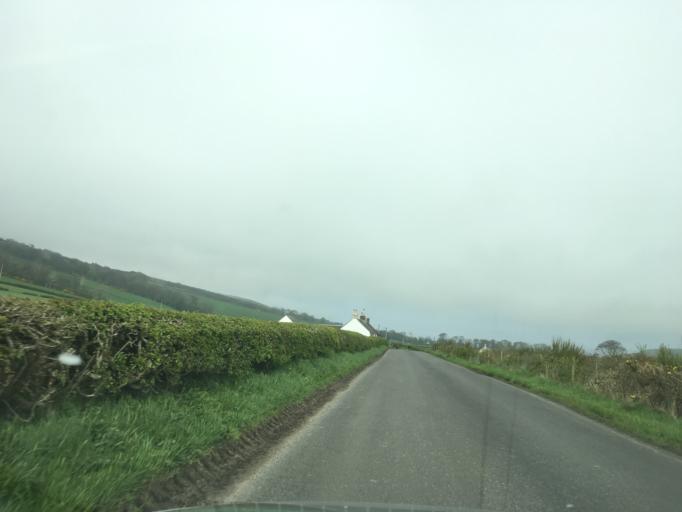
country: GB
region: Scotland
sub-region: Argyll and Bute
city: Port Bannatyne
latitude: 55.8536
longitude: -5.1333
